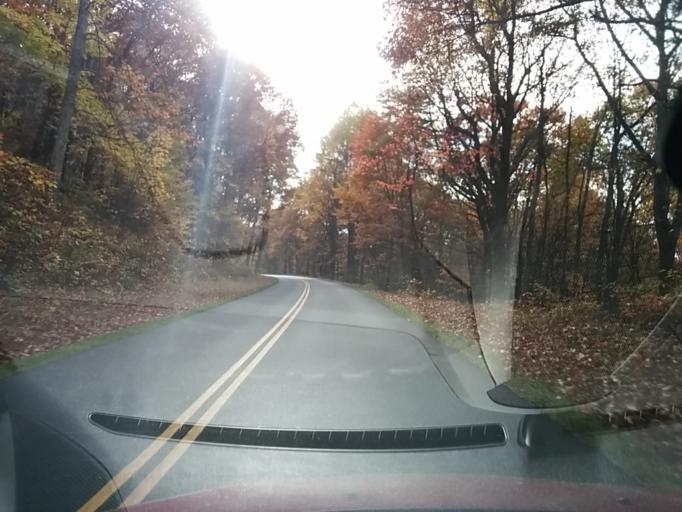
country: US
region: Virginia
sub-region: Nelson County
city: Nellysford
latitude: 37.8907
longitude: -79.0000
